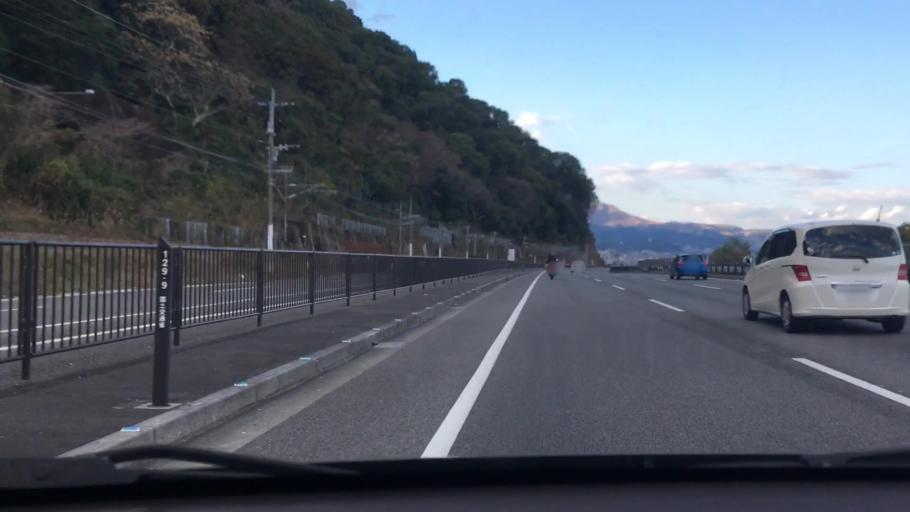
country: JP
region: Oita
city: Beppu
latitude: 33.2606
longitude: 131.5313
